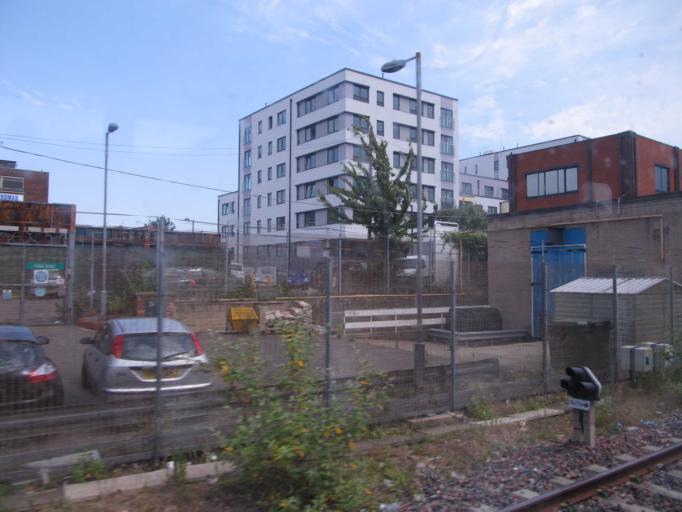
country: GB
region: England
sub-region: Slough
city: Slough
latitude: 51.5133
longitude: -0.5954
